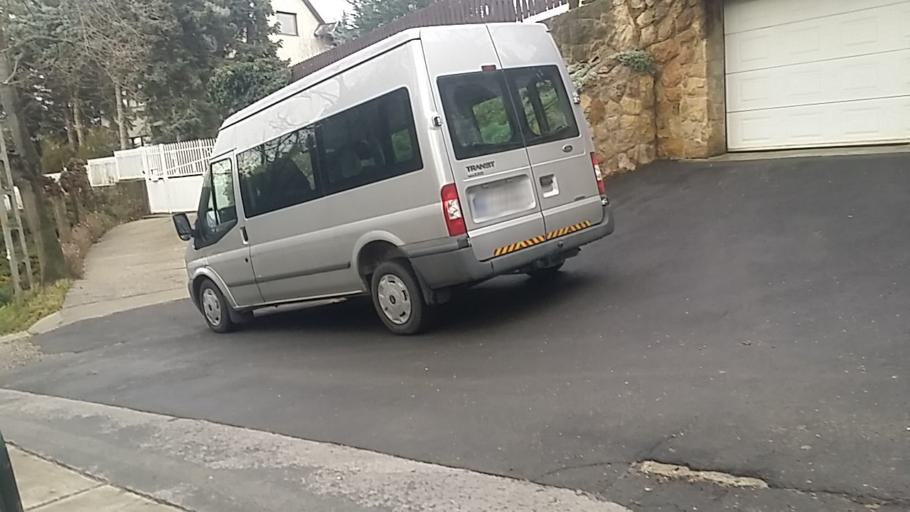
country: HU
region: Pest
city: Budakeszi
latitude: 47.5075
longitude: 18.9305
